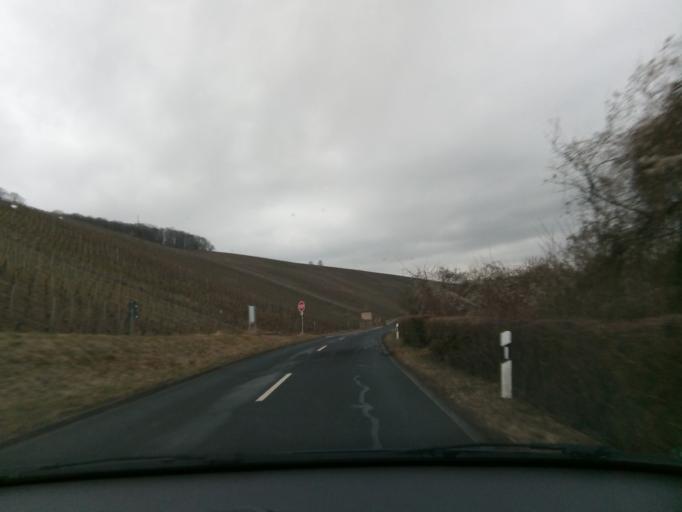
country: DE
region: Bavaria
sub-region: Regierungsbezirk Unterfranken
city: Nordheim
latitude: 49.8524
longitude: 10.1674
